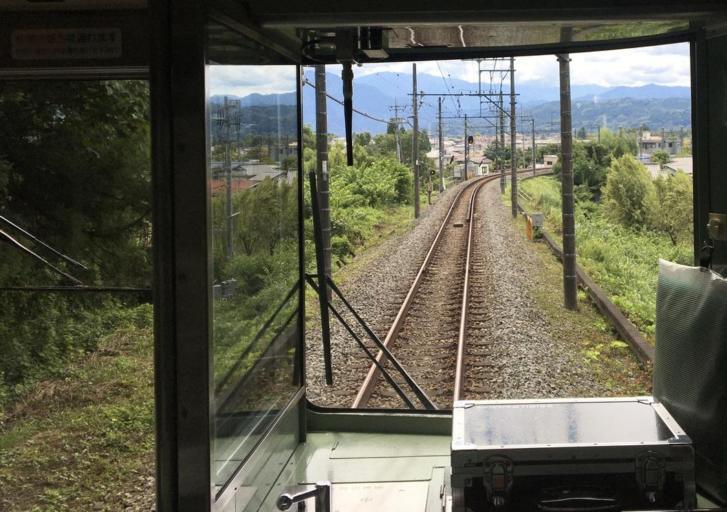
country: JP
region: Saitama
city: Chichibu
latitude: 35.9845
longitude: 139.0862
